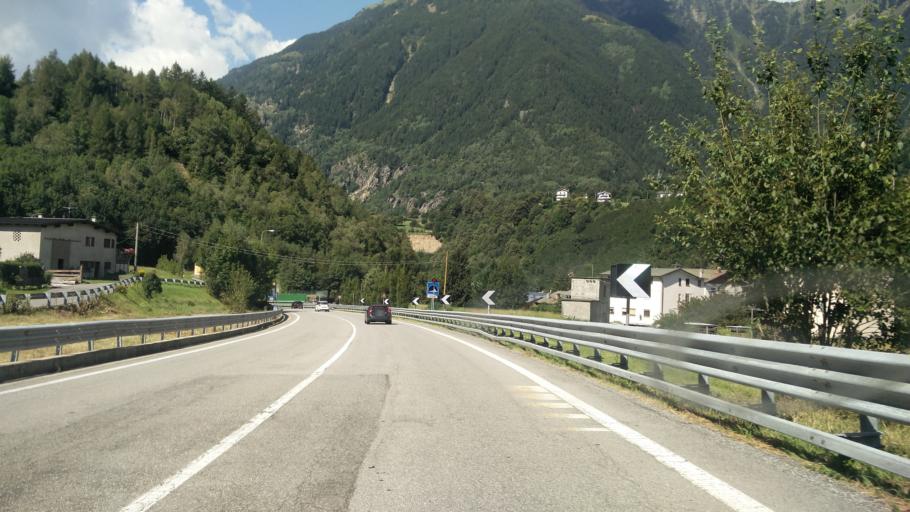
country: IT
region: Lombardy
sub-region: Provincia di Sondrio
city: Sondalo
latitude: 46.3254
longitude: 10.3243
